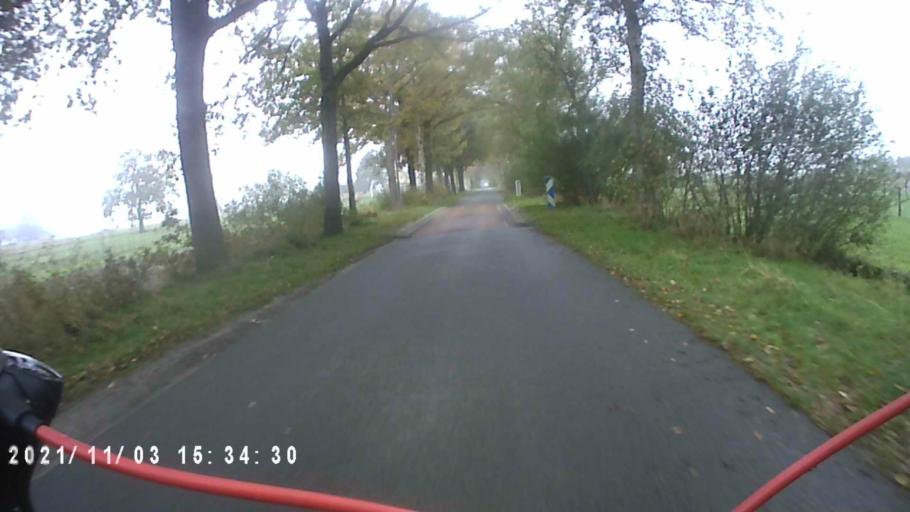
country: NL
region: Groningen
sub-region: Gemeente Leek
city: Leek
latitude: 53.1204
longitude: 6.3630
